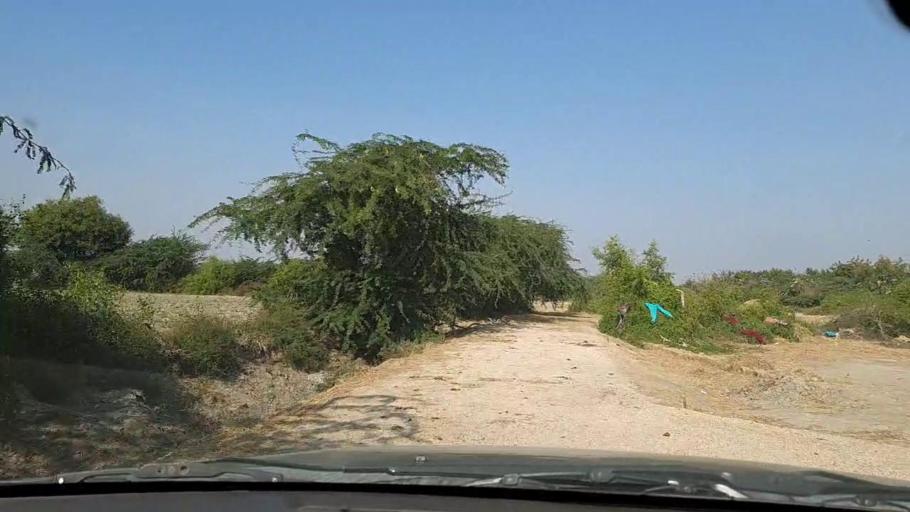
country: PK
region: Sindh
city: Chuhar Jamali
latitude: 24.3994
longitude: 67.8234
